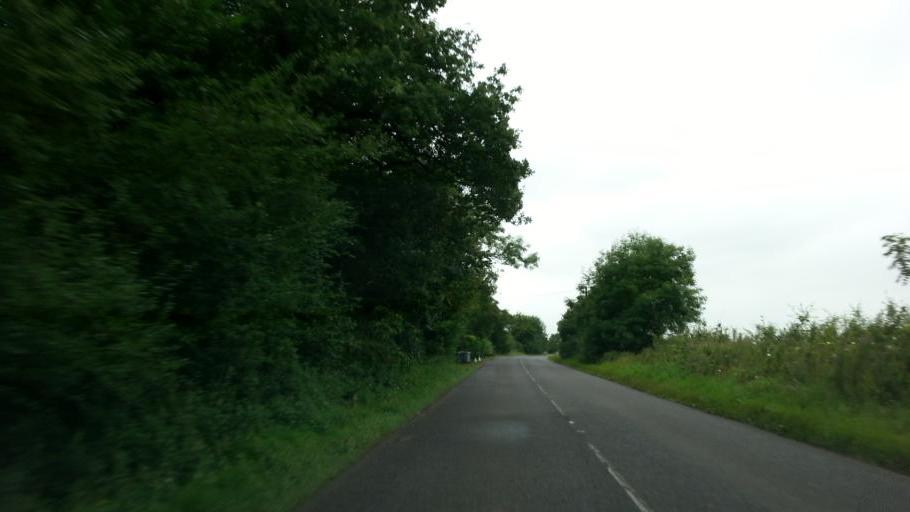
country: GB
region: England
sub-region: Nottinghamshire
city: Farnsfield
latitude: 53.0620
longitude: -1.0253
